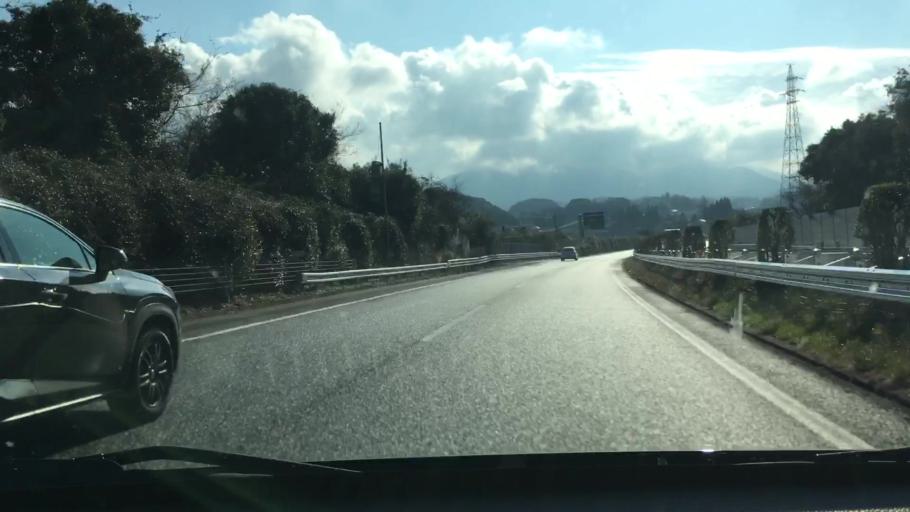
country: JP
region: Kumamoto
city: Matsubase
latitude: 32.5836
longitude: 130.7159
